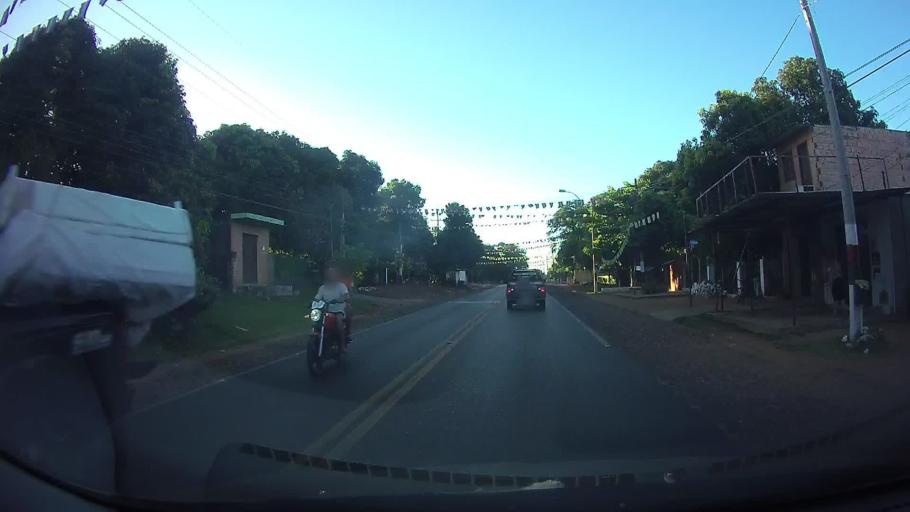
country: PY
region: Central
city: Aregua
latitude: -25.3018
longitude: -57.4053
